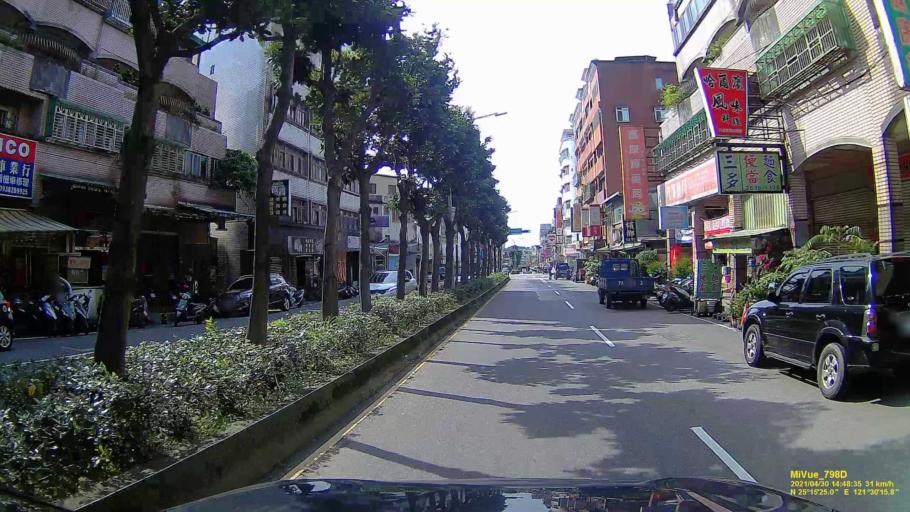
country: TW
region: Taipei
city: Taipei
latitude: 25.2571
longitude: 121.5043
